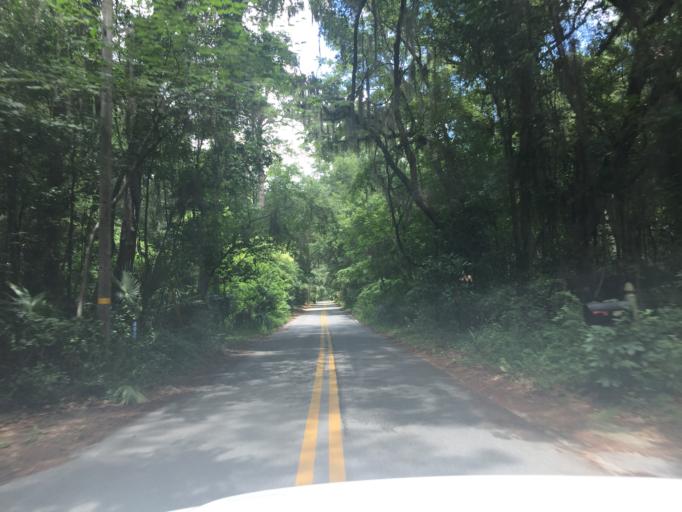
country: US
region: Georgia
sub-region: Chatham County
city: Montgomery
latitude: 31.9409
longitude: -81.1163
